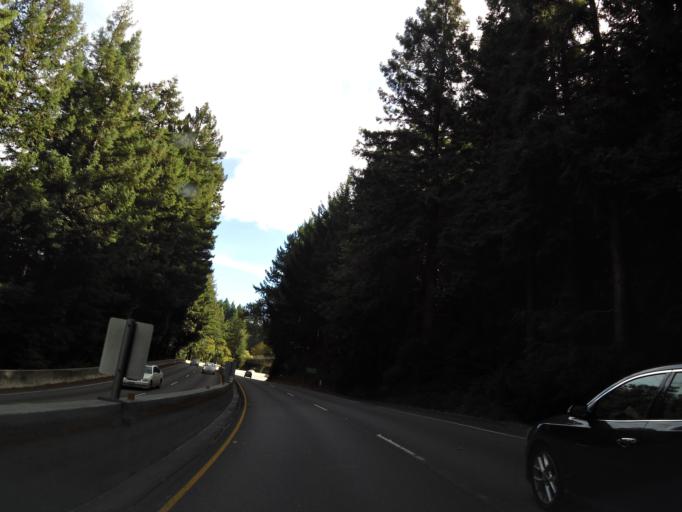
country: US
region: California
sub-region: Santa Clara County
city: Lexington Hills
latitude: 37.1467
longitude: -121.9877
